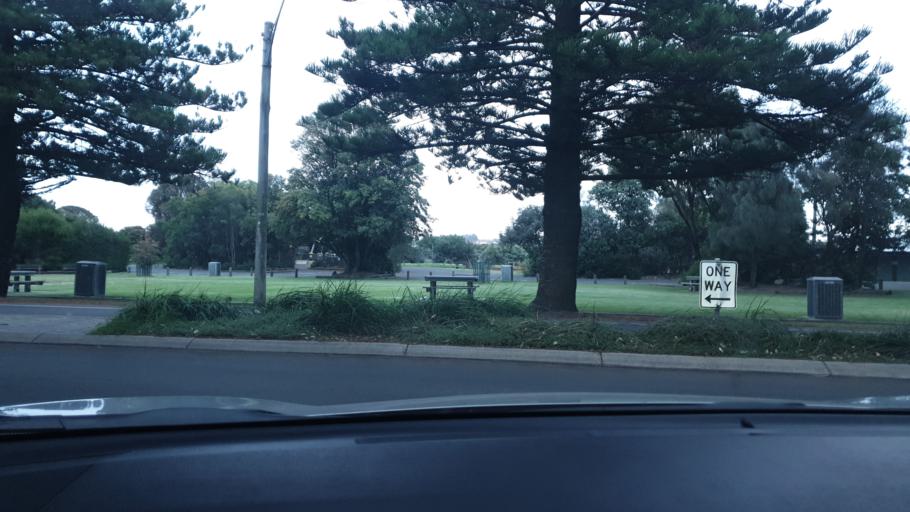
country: AU
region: Victoria
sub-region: Warrnambool
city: Warrnambool
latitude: -38.3937
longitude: 142.4784
